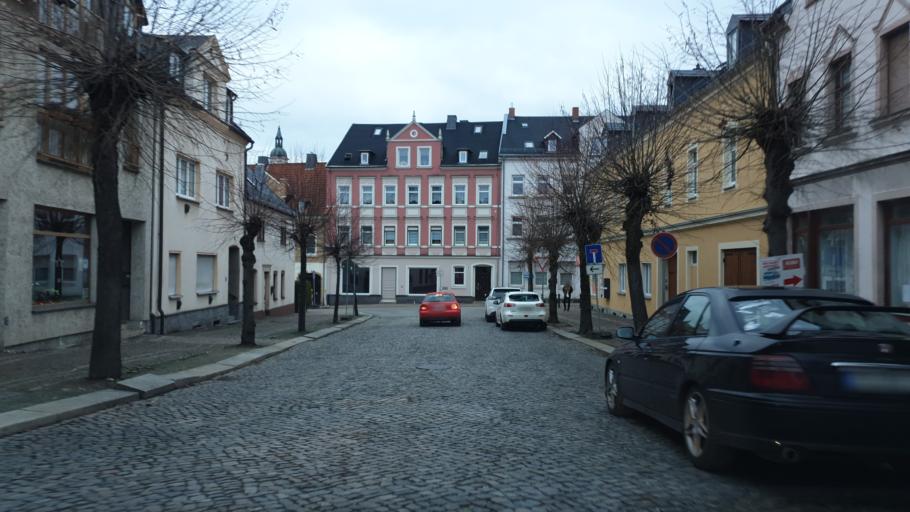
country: DE
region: Saxony
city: Lichtenstein
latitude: 50.7532
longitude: 12.6326
